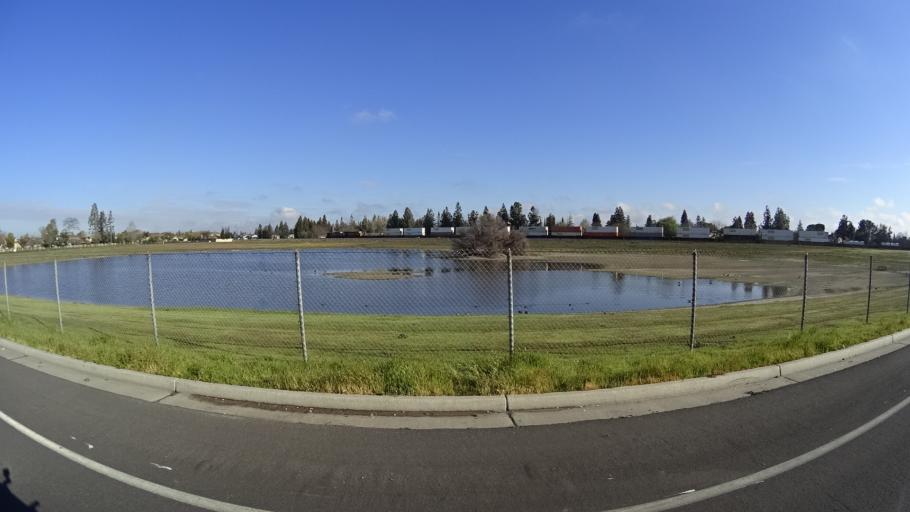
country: US
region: California
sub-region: Fresno County
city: West Park
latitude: 36.8153
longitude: -119.8560
